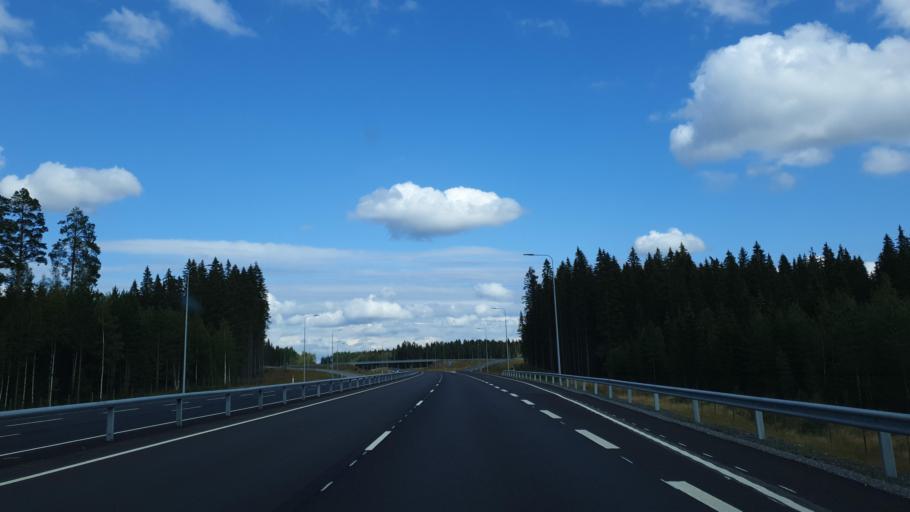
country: FI
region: Southern Savonia
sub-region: Mikkeli
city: Mikkeli
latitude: 61.7346
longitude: 27.4088
